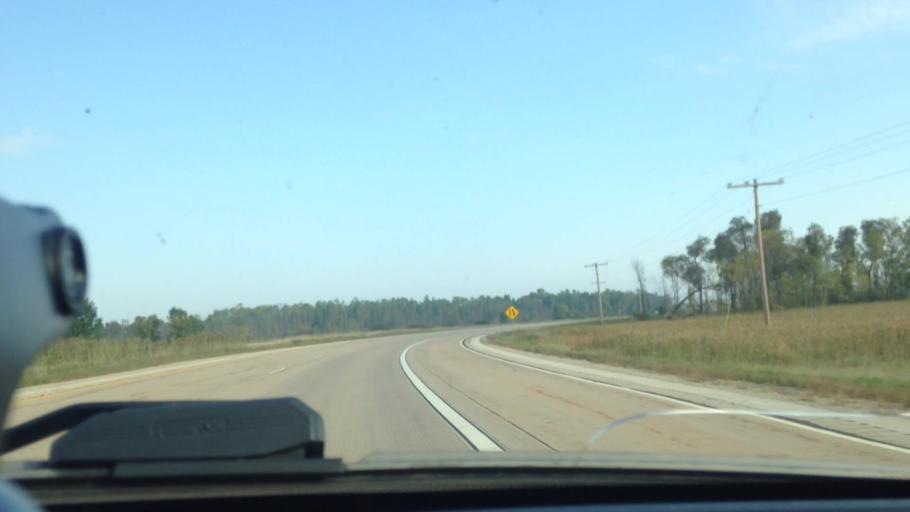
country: US
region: Wisconsin
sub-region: Oconto County
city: Oconto Falls
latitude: 44.9844
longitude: -88.0481
